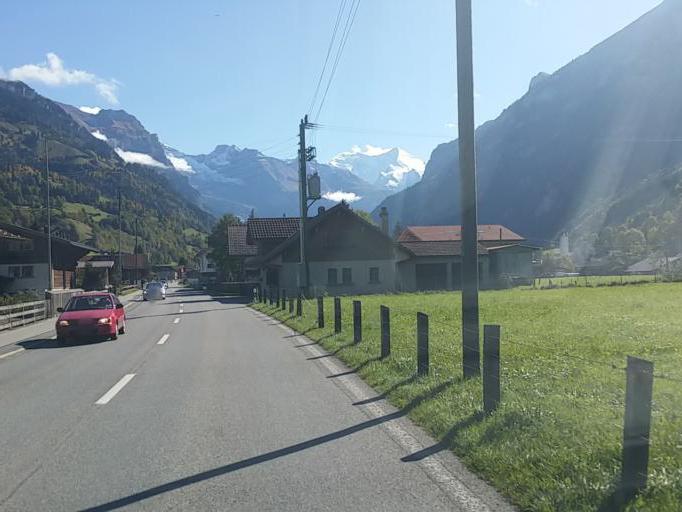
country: CH
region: Bern
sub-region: Frutigen-Niedersimmental District
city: Frutigen
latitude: 46.5698
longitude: 7.6546
